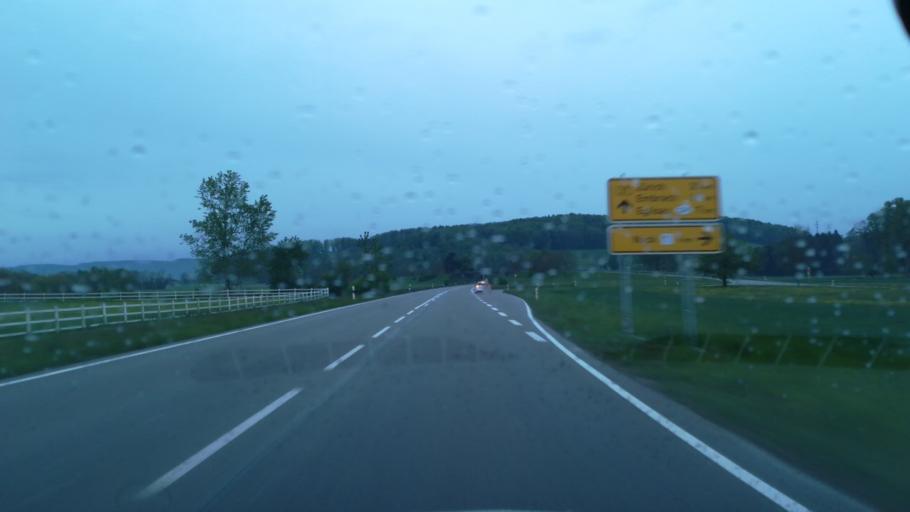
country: DE
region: Baden-Wuerttemberg
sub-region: Freiburg Region
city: Lottstetten
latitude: 47.6220
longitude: 8.5780
